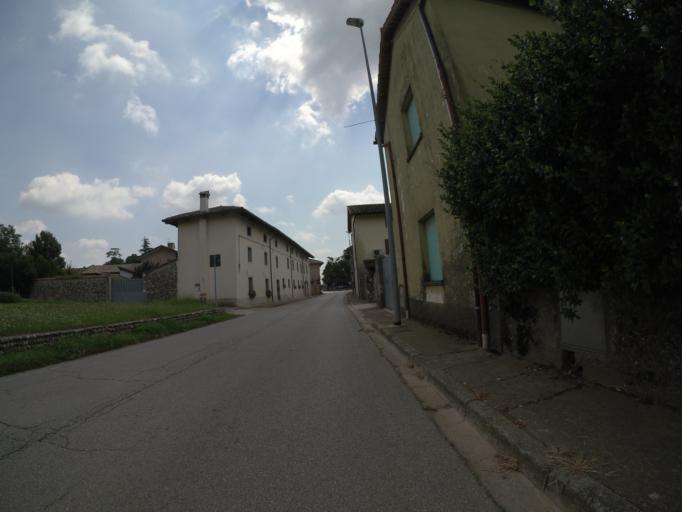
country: IT
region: Friuli Venezia Giulia
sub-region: Provincia di Udine
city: Basiliano
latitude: 46.0137
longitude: 13.0685
